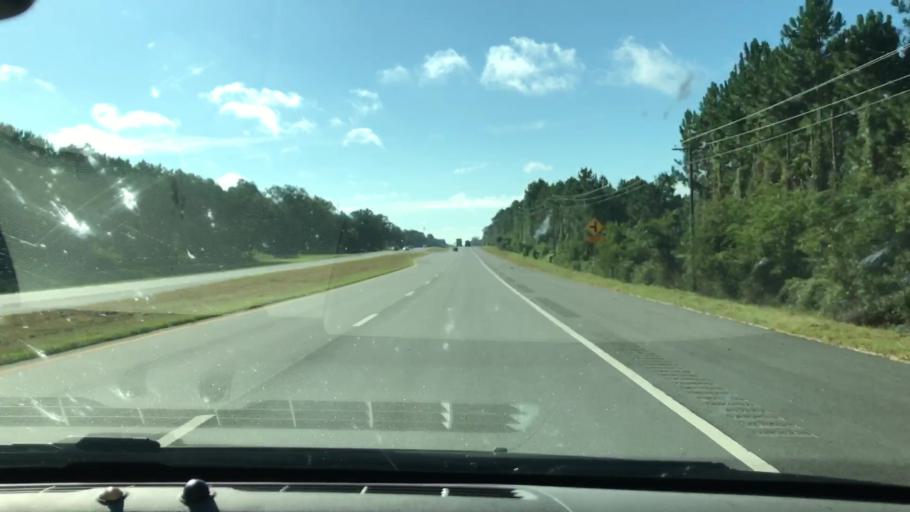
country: US
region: Georgia
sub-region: Lee County
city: Leesburg
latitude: 31.6727
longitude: -84.2907
